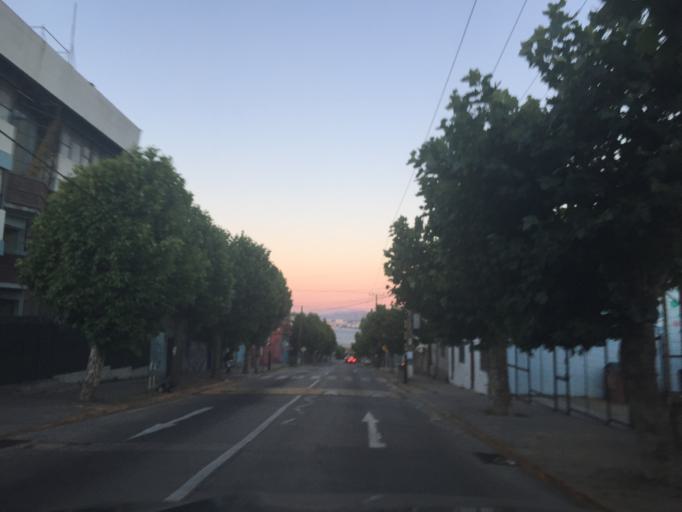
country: CL
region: Valparaiso
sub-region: Provincia de Valparaiso
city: Valparaiso
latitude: -33.0324
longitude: -71.6396
